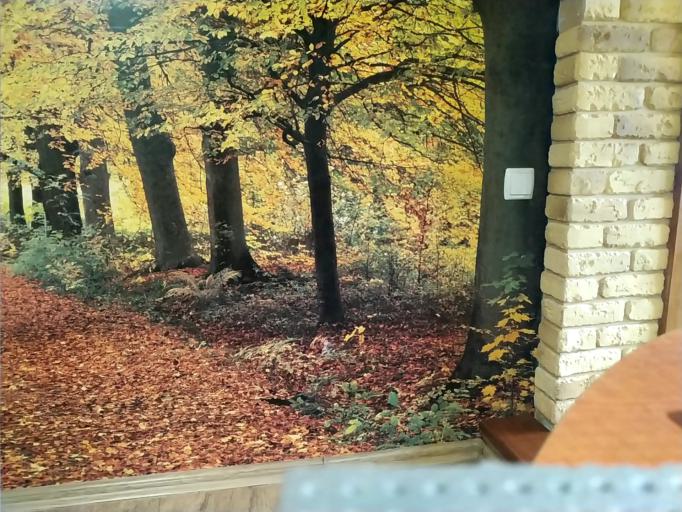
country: RU
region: Tverskaya
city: Kalashnikovo
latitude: 57.2739
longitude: 35.2685
